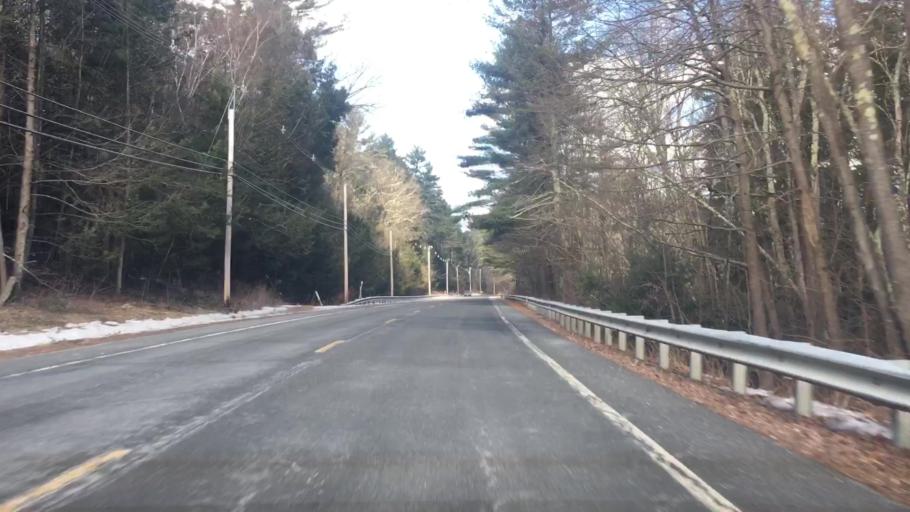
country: US
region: Massachusetts
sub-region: Hampden County
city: Brimfield
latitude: 42.0968
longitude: -72.2018
